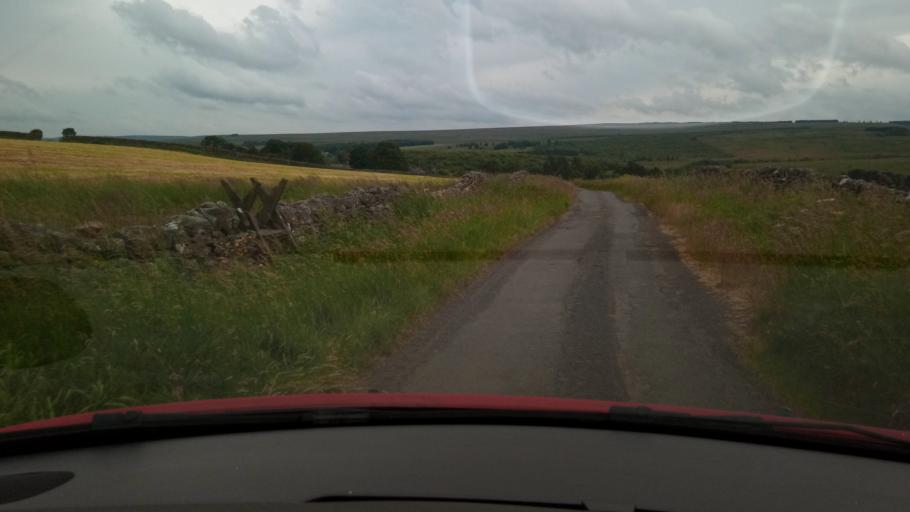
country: GB
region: England
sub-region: Northumberland
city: Rochester
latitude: 55.2808
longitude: -2.2645
